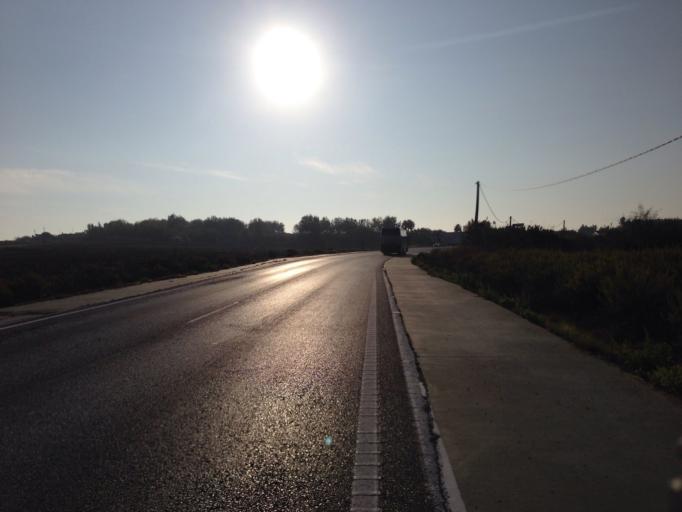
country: ES
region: Andalusia
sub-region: Provincia de Cadiz
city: Conil de la Frontera
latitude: 36.2947
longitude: -6.0983
